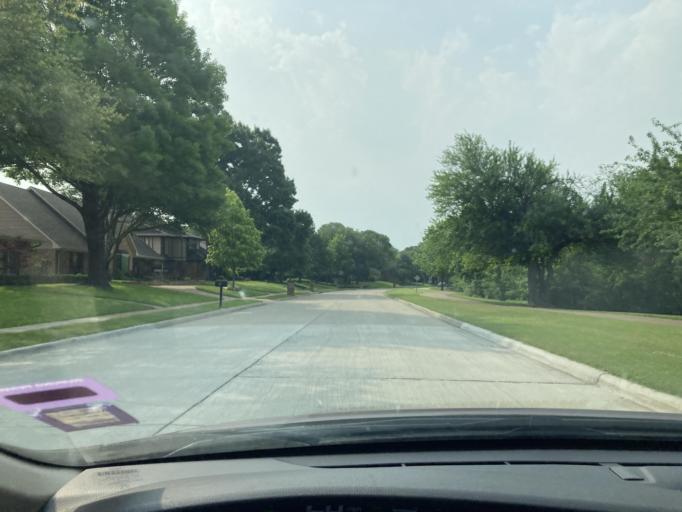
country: US
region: Texas
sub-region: Collin County
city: Plano
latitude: 33.0542
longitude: -96.7287
